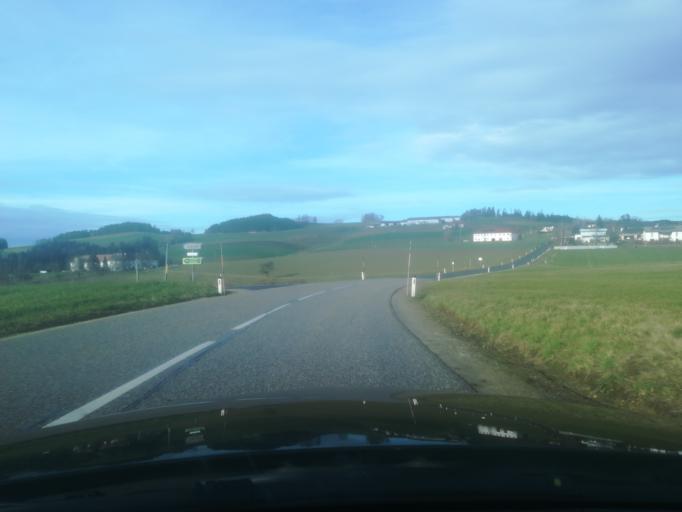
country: AT
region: Upper Austria
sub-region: Politischer Bezirk Perg
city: Perg
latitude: 48.3381
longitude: 14.6221
